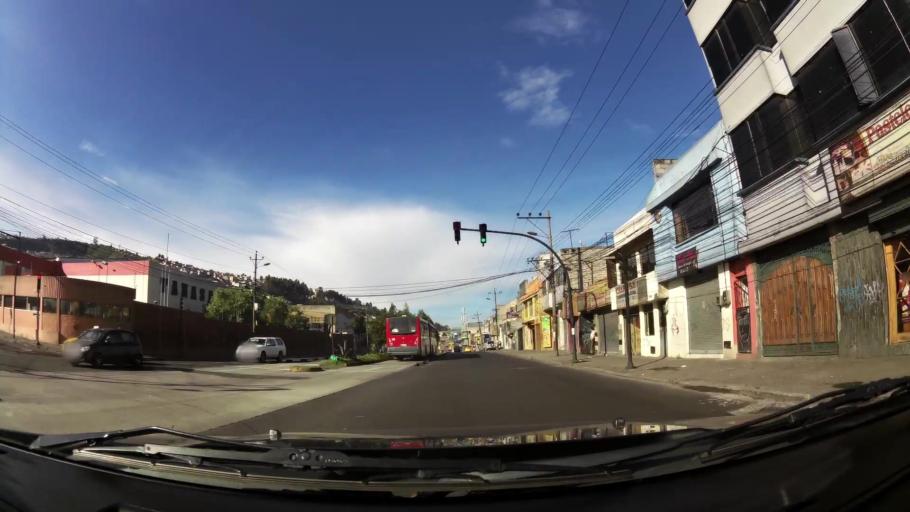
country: EC
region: Pichincha
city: Quito
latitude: -0.2729
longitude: -78.5295
